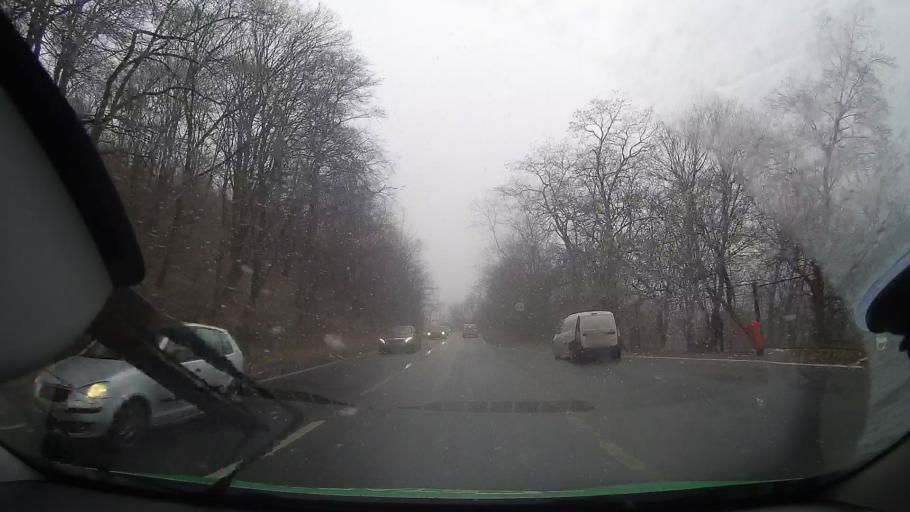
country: RO
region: Sibiu
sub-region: Municipiul Medias
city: Medias
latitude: 46.1833
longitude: 24.3341
